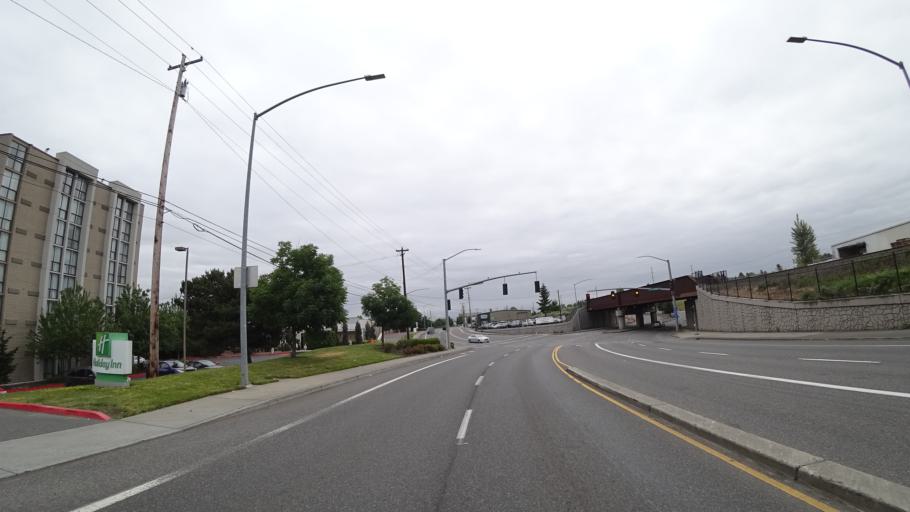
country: US
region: Oregon
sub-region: Multnomah County
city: Lents
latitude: 45.5644
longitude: -122.5761
